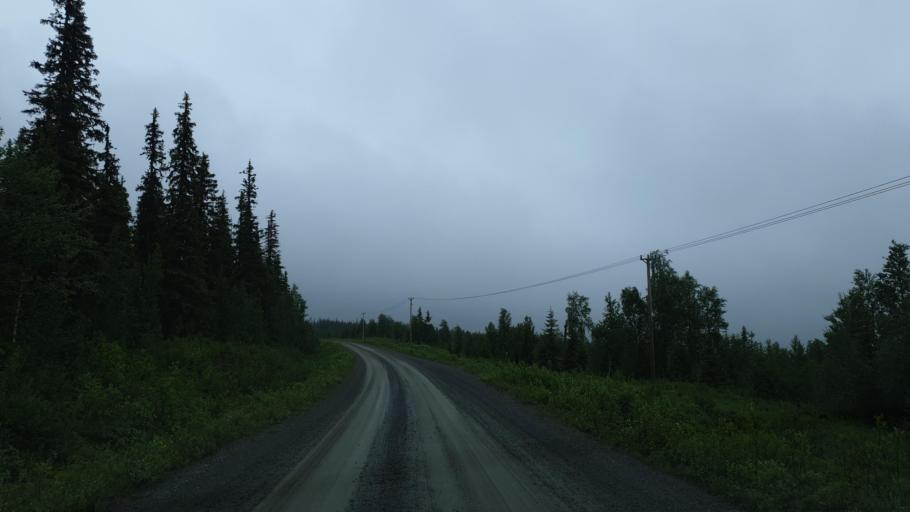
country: SE
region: Vaesterbotten
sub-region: Vilhelmina Kommun
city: Sjoberg
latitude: 65.3228
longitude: 15.9333
